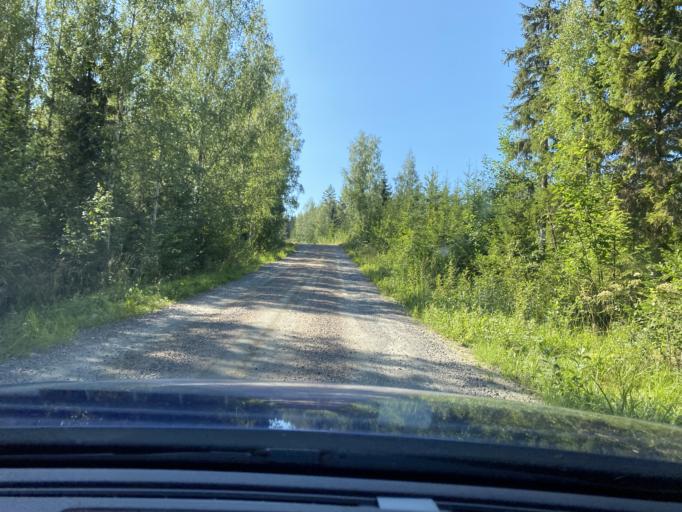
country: FI
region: Central Finland
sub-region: Jaemsae
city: Jaemsae
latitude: 61.8655
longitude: 25.3983
